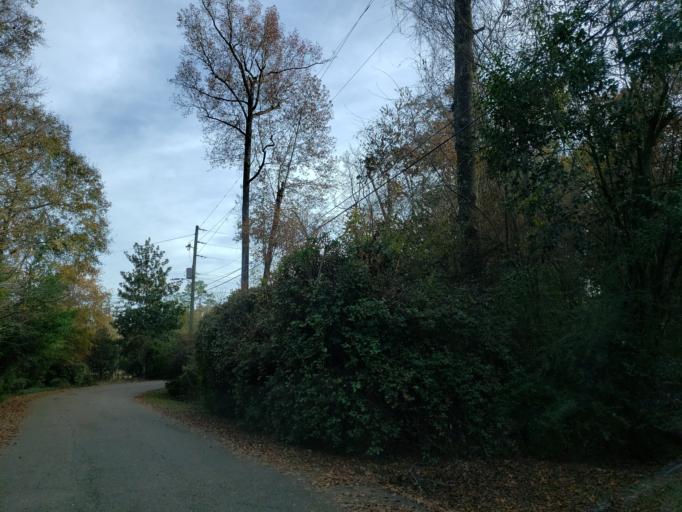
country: US
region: Mississippi
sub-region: Lamar County
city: West Hattiesburg
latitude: 31.3219
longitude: -89.3370
